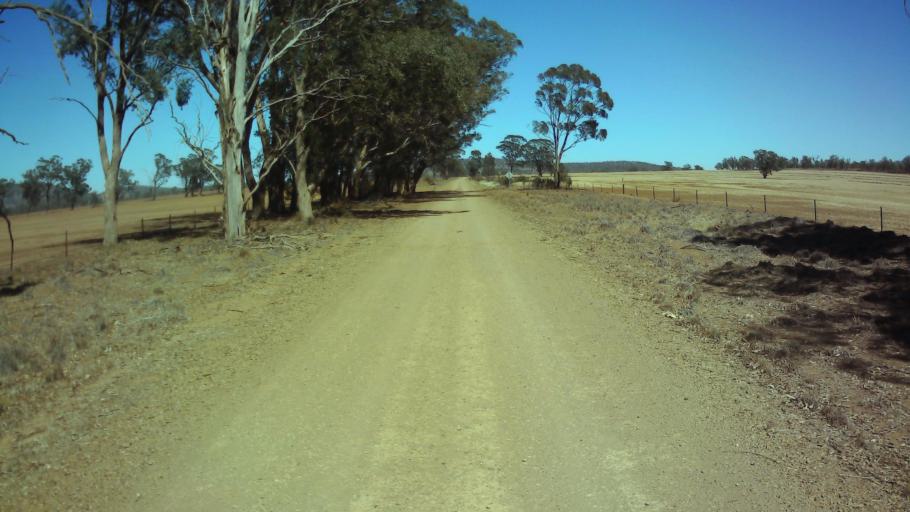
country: AU
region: New South Wales
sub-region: Weddin
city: Grenfell
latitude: -33.7075
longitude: 147.9966
